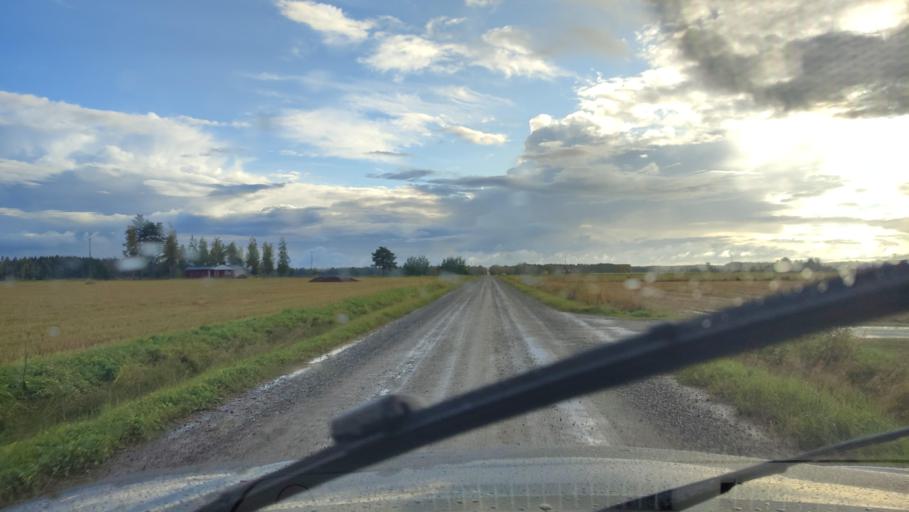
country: FI
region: Southern Ostrobothnia
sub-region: Suupohja
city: Karijoki
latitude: 62.3308
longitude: 21.5837
